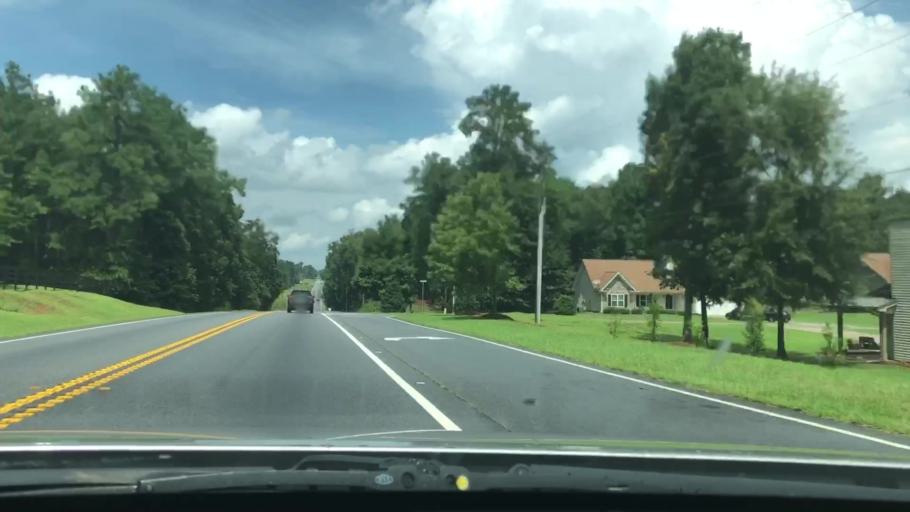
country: US
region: Georgia
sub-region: Lamar County
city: Barnesville
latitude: 33.1020
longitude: -84.1548
